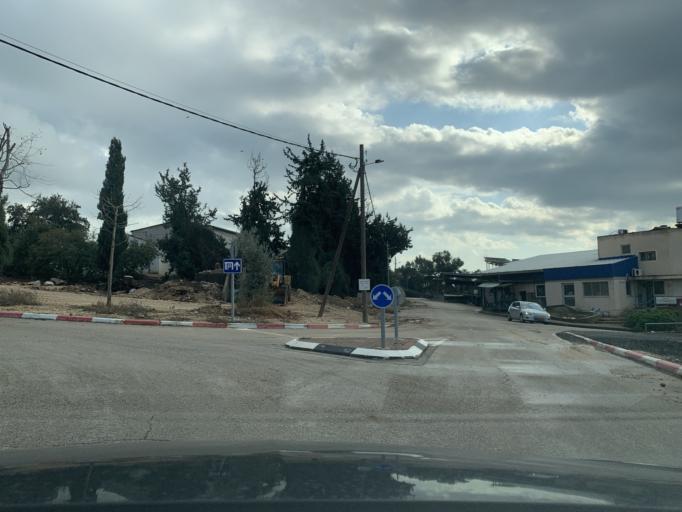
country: IL
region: Central District
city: Rosh Ha'Ayin
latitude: 32.0599
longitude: 34.9486
